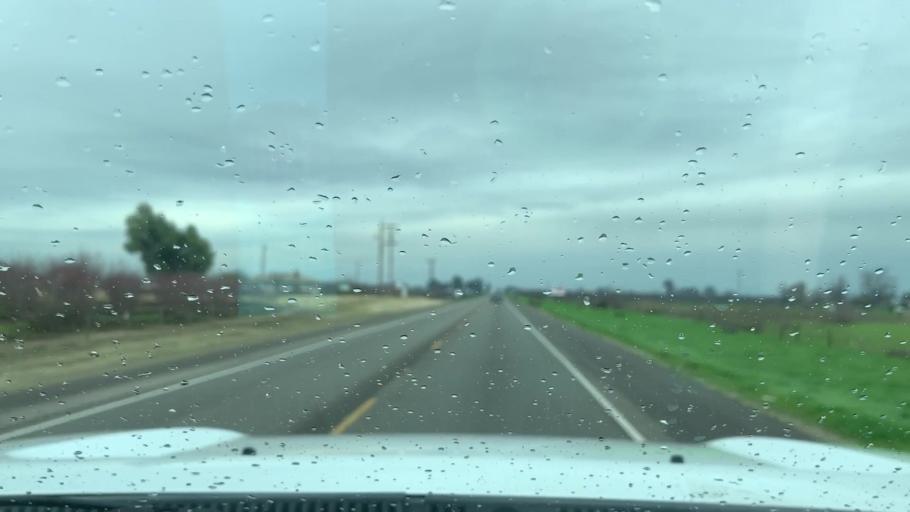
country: US
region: California
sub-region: Fresno County
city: Riverdale
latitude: 36.4216
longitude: -119.8031
